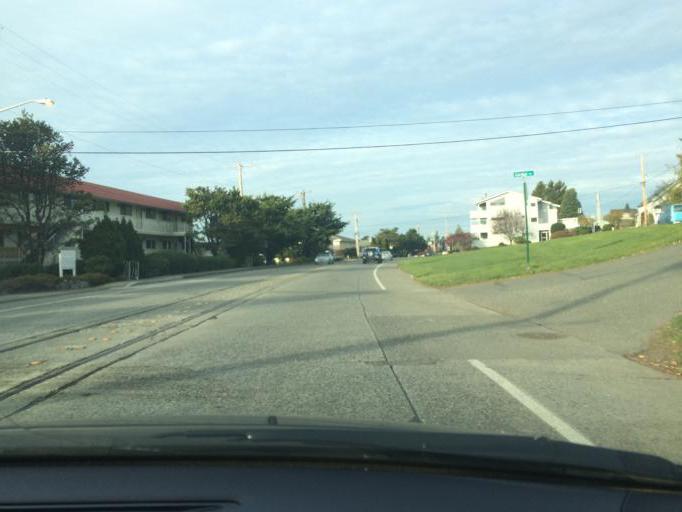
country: US
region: Washington
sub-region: Whatcom County
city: Bellingham
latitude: 48.7231
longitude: -122.5035
